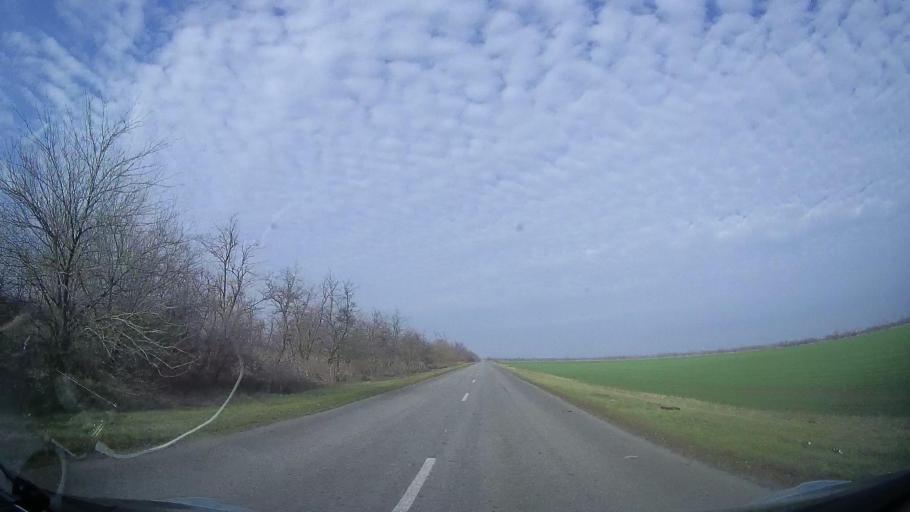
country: RU
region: Rostov
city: Gigant
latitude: 46.8660
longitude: 41.2771
